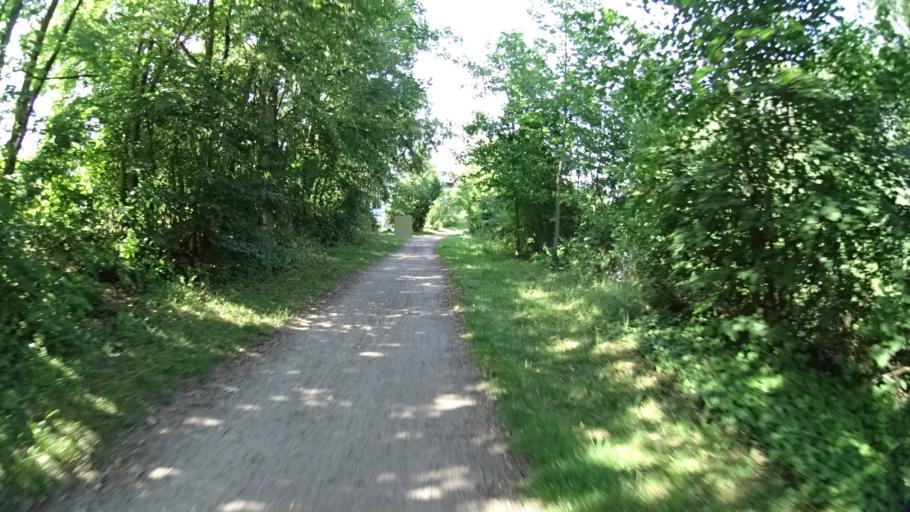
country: DE
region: Lower Saxony
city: Lueneburg
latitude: 53.2552
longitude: 10.4131
